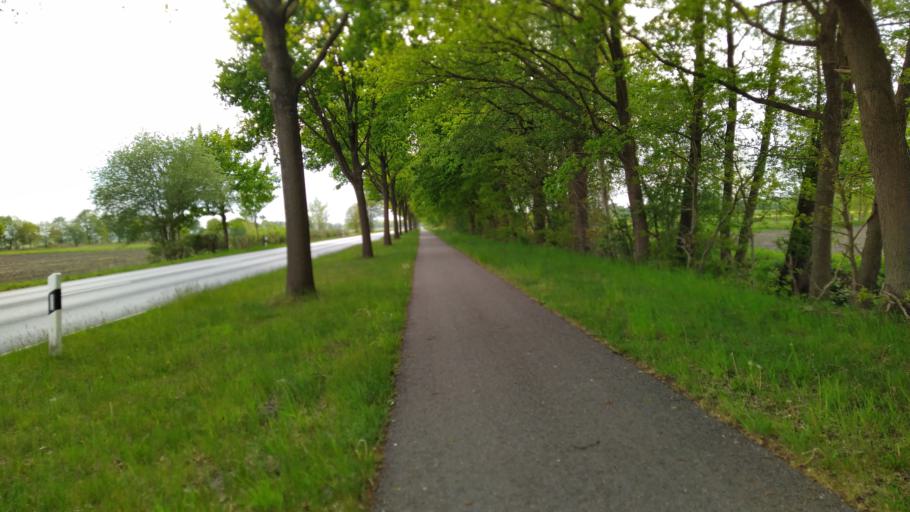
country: DE
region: Lower Saxony
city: Tarmstedt
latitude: 53.2150
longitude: 9.0537
